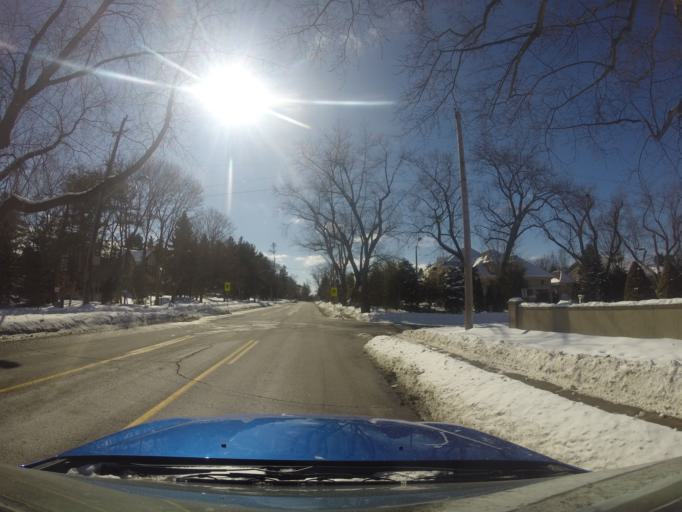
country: CA
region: Ontario
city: Burlington
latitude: 43.3431
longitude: -79.7652
